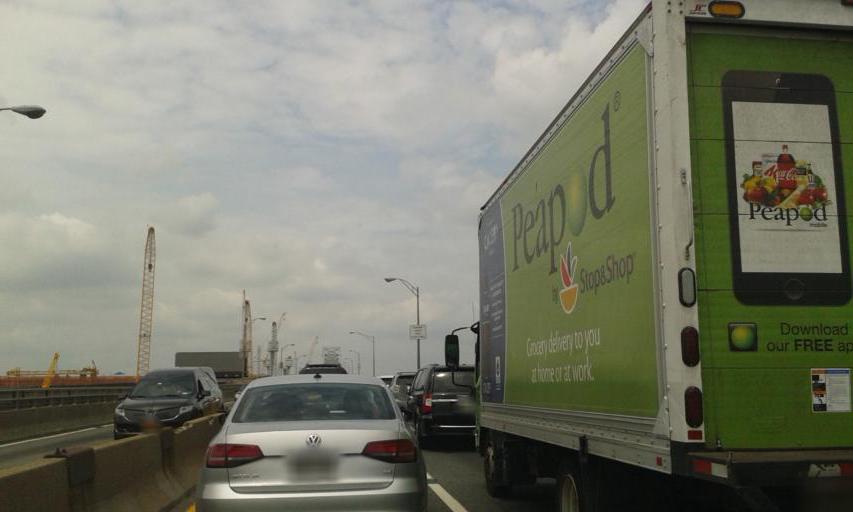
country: US
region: New York
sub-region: Richmond County
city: Bloomfield
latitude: 40.6311
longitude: -74.1880
